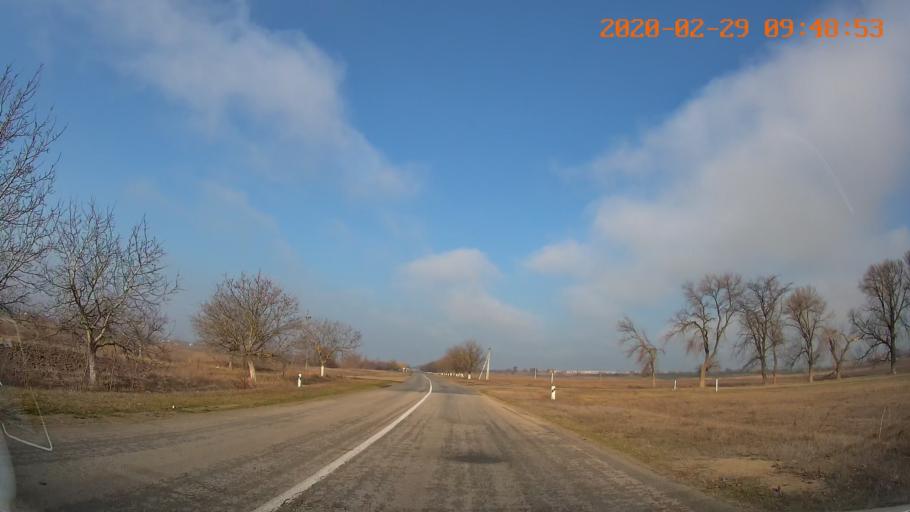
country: MD
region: Telenesti
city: Crasnoe
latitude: 46.6931
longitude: 29.7807
